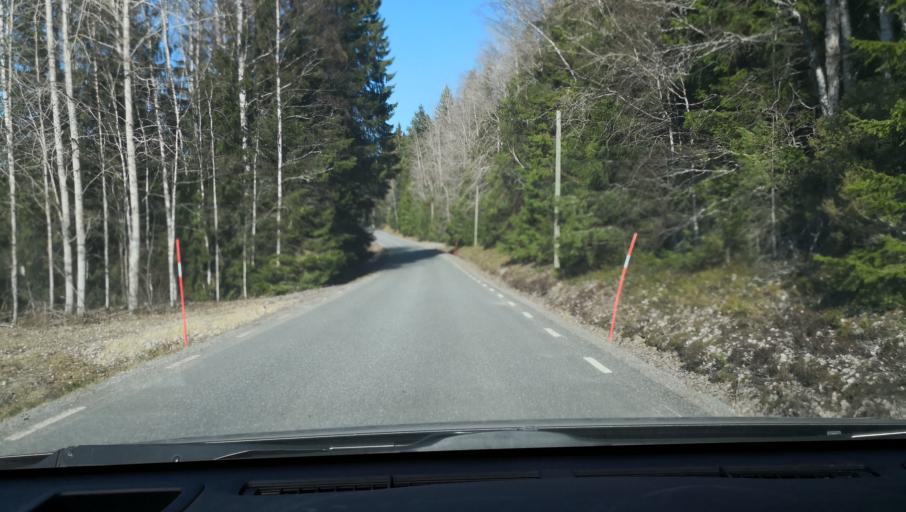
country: SE
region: Vaestmanland
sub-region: Sala Kommun
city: Sala
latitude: 59.9767
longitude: 16.4711
